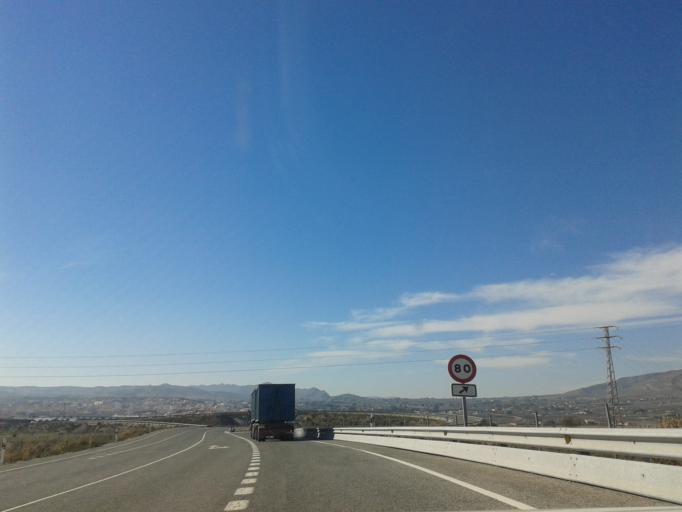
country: ES
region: Castille-La Mancha
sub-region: Provincia de Albacete
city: Caudete
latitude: 38.7181
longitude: -0.9637
